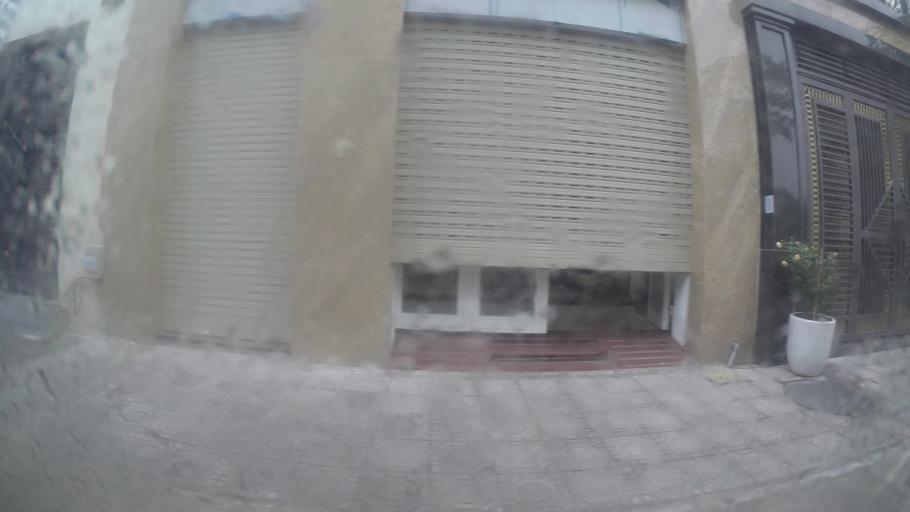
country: VN
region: Ha Noi
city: Cau Giay
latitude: 21.0198
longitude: 105.7882
